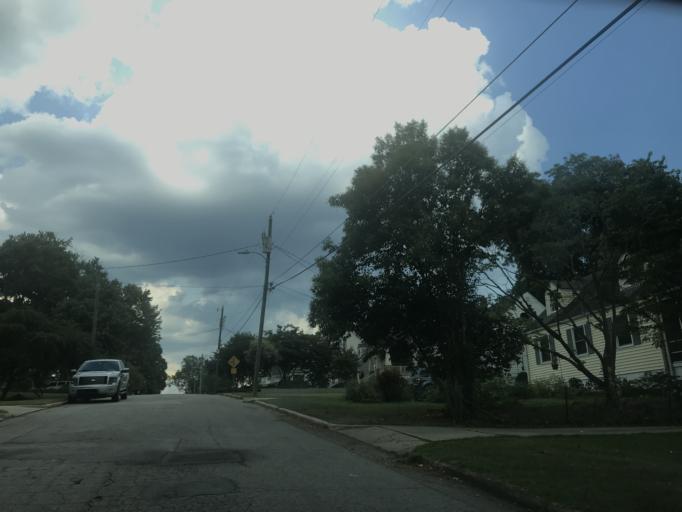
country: US
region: North Carolina
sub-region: Wake County
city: Raleigh
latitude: 35.8099
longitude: -78.6300
